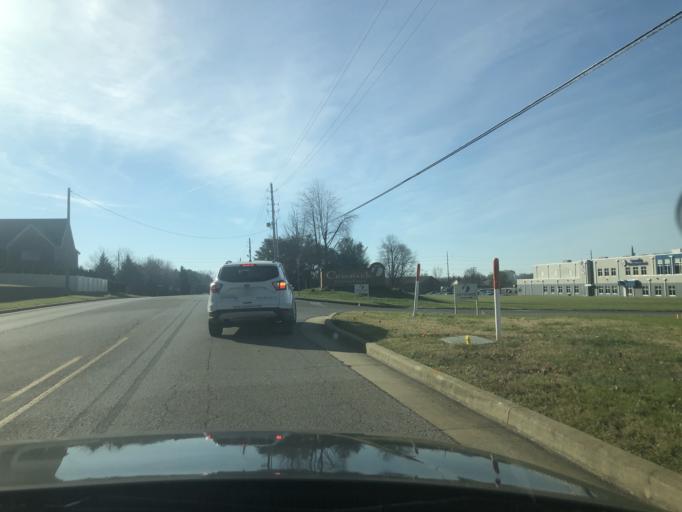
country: US
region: Indiana
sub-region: Warrick County
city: Newburgh
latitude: 37.9723
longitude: -87.4412
